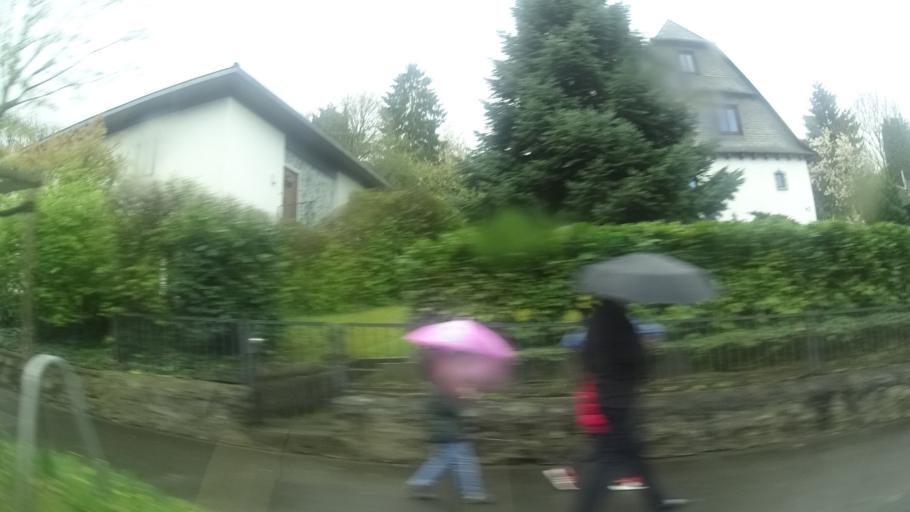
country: DE
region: Hesse
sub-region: Regierungsbezirk Giessen
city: Wetzlar
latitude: 50.5555
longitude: 8.5117
